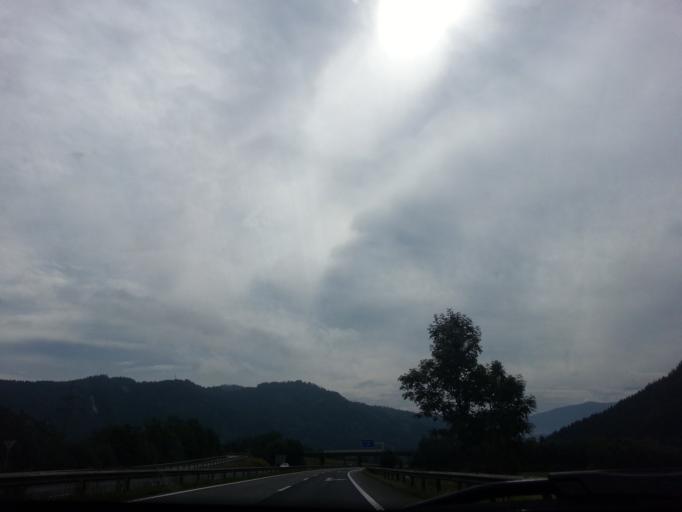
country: AT
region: Styria
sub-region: Politischer Bezirk Leoben
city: Traboch
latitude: 47.3713
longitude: 14.9886
